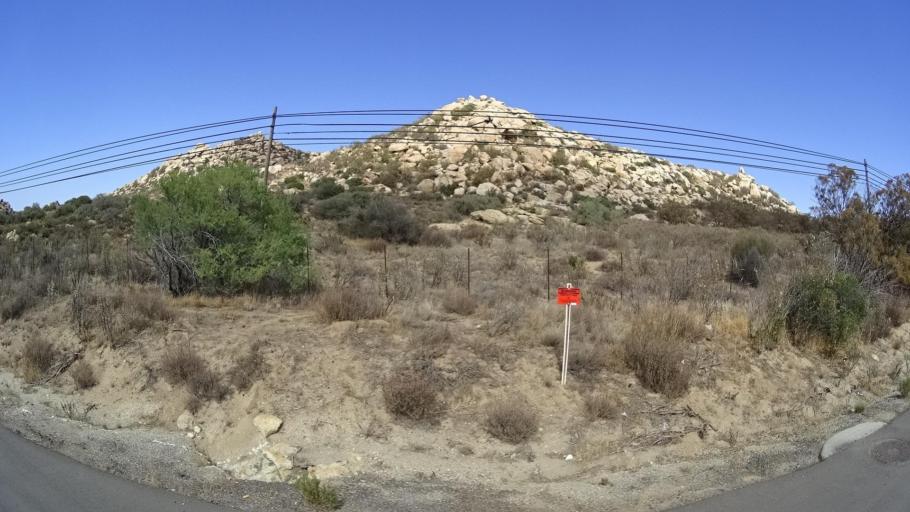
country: MX
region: Baja California
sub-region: Tecate
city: Cereso del Hongo
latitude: 32.6458
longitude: -116.2377
